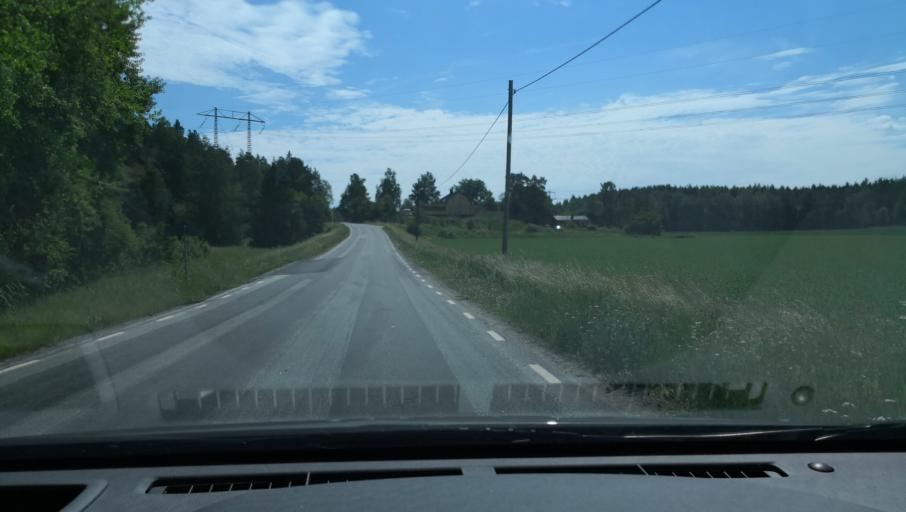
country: SE
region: Uppsala
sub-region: Habo Kommun
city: Balsta
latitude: 59.6619
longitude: 17.4499
